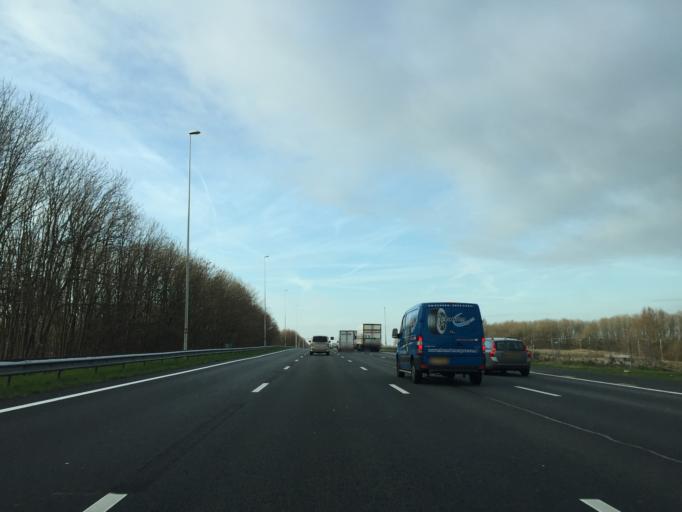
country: NL
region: Utrecht
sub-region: Gemeente Woerden
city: Woerden
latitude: 52.0699
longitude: 4.8776
